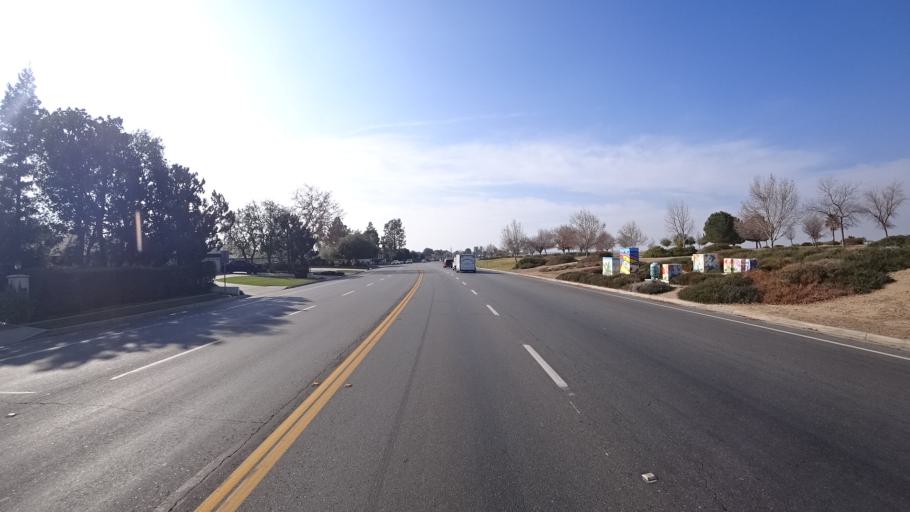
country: US
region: California
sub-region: Kern County
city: Oildale
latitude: 35.4097
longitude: -118.9817
